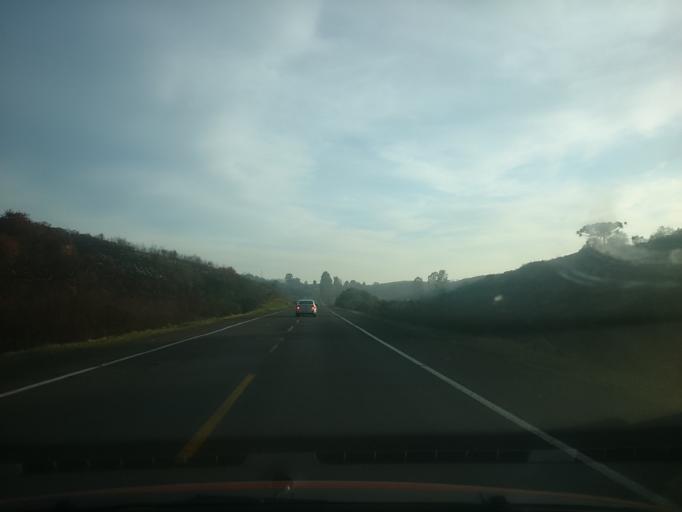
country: BR
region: Rio Grande do Sul
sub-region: Vacaria
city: Vacaria
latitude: -28.3202
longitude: -50.8051
